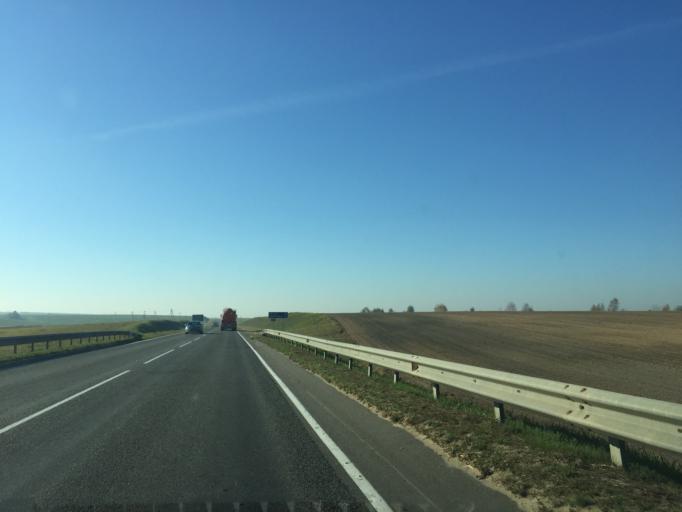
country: BY
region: Mogilev
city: Buynichy
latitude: 53.9446
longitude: 30.2165
